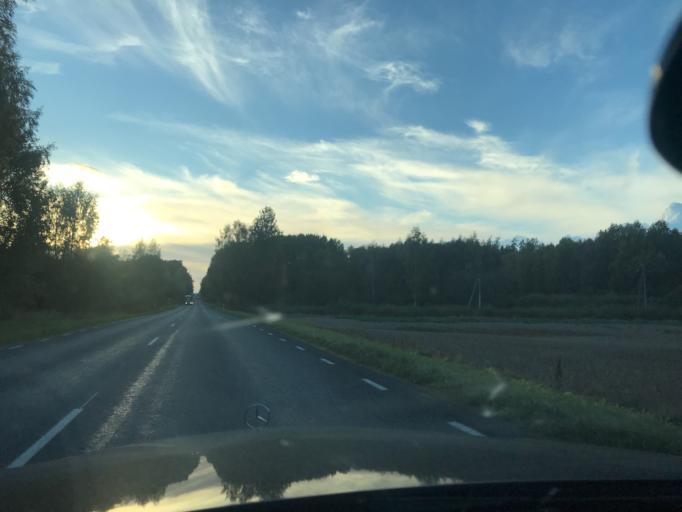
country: EE
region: Vorumaa
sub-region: Antsla vald
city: Vana-Antsla
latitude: 57.8796
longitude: 26.6971
